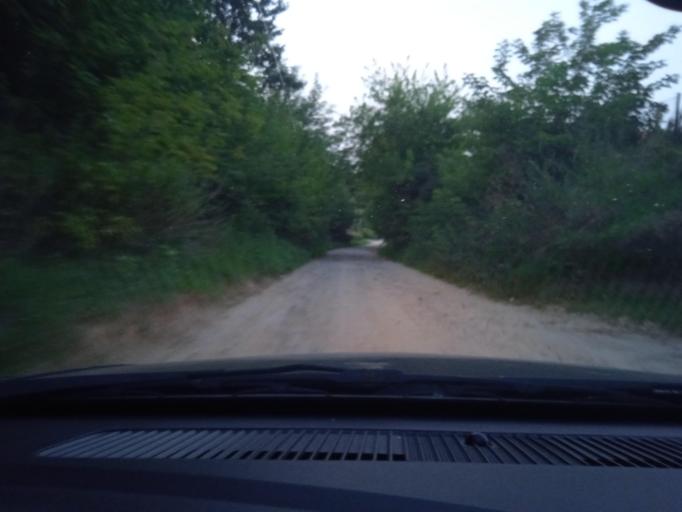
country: PL
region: Masovian Voivodeship
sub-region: Powiat nowodworski
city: Pomiechowek
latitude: 52.4896
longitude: 20.7047
